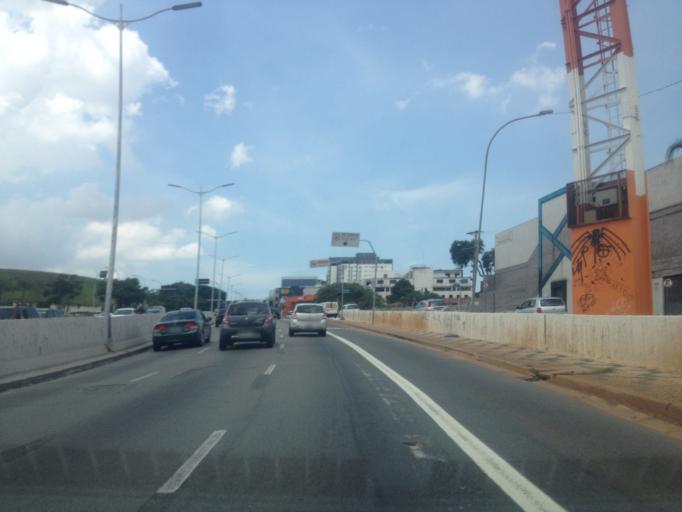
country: BR
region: Sao Paulo
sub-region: Sao Paulo
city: Sao Paulo
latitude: -23.6185
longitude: -46.6622
